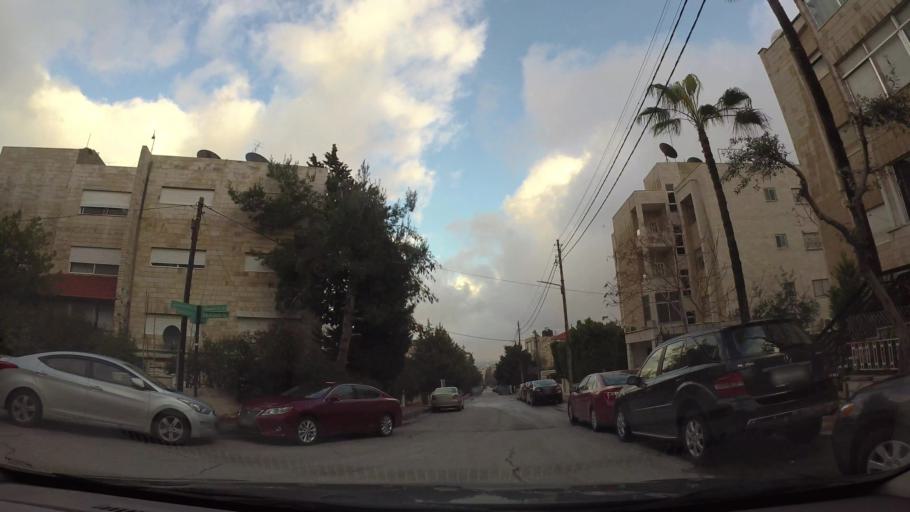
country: JO
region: Amman
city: Amman
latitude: 31.9561
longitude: 35.8873
